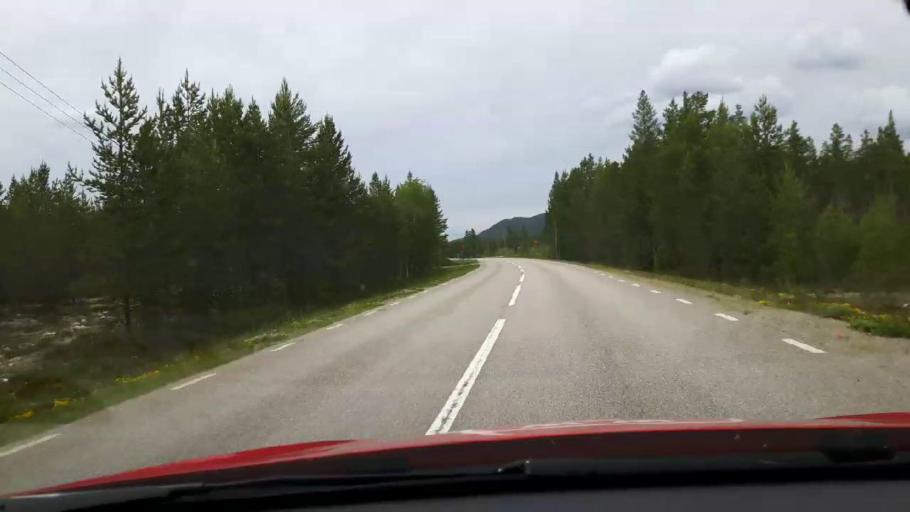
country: SE
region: Jaemtland
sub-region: Harjedalens Kommun
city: Sveg
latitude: 62.4044
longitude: 13.7351
